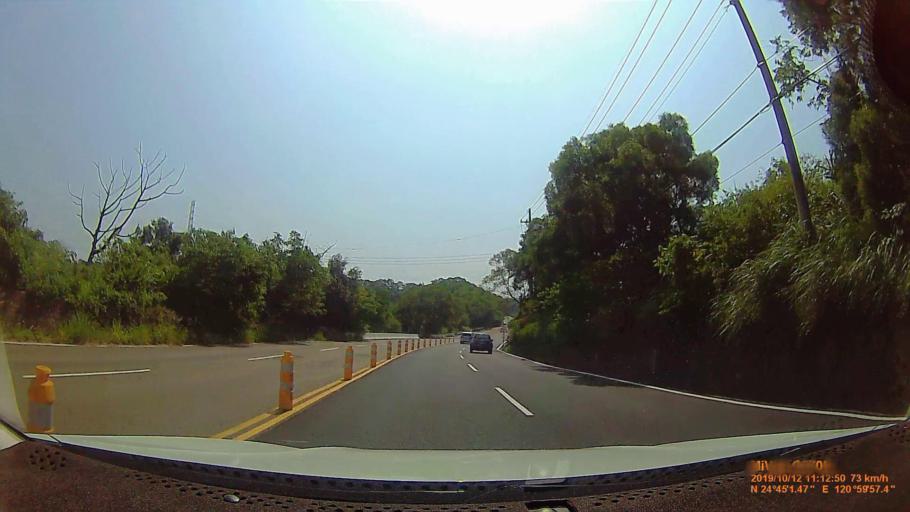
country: TW
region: Taiwan
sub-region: Hsinchu
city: Hsinchu
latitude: 24.7505
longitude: 120.9992
